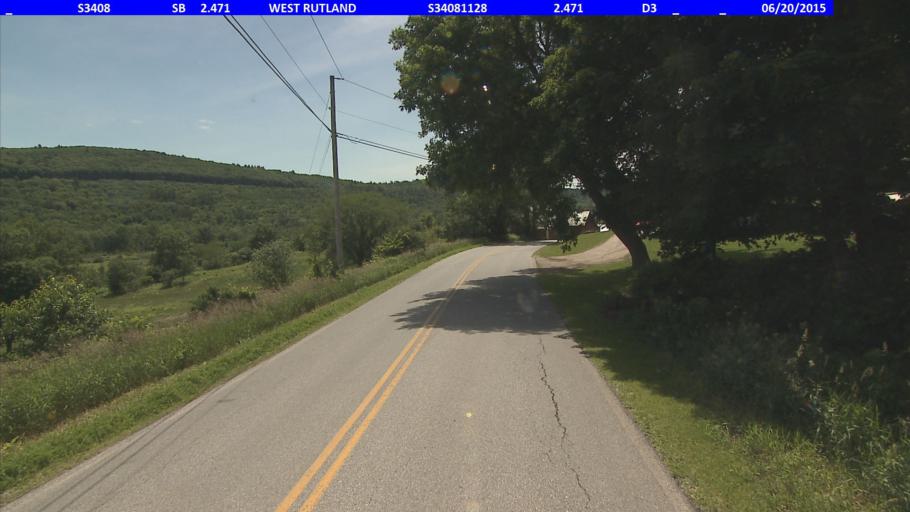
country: US
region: Vermont
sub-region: Rutland County
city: West Rutland
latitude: 43.6449
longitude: -73.0700
